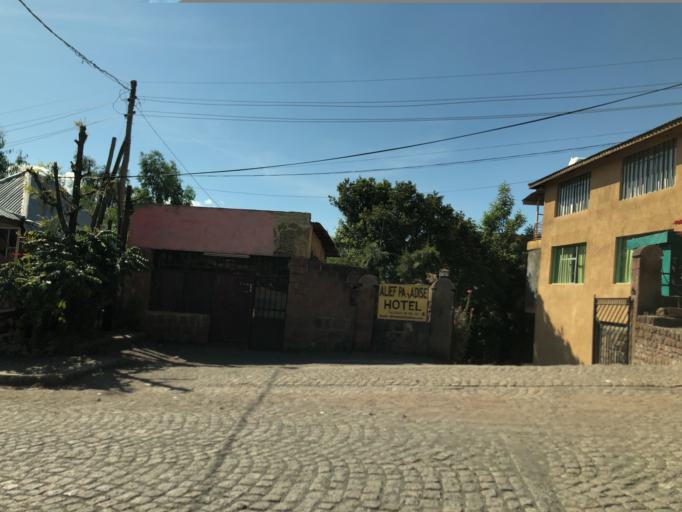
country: ET
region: Amhara
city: Lalibela
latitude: 12.0286
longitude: 39.0426
